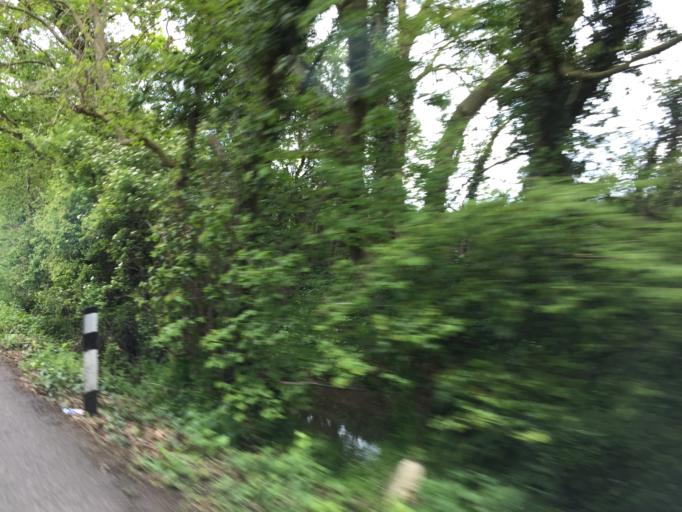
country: GB
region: England
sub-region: Gloucestershire
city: Stonehouse
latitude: 51.7744
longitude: -2.2961
